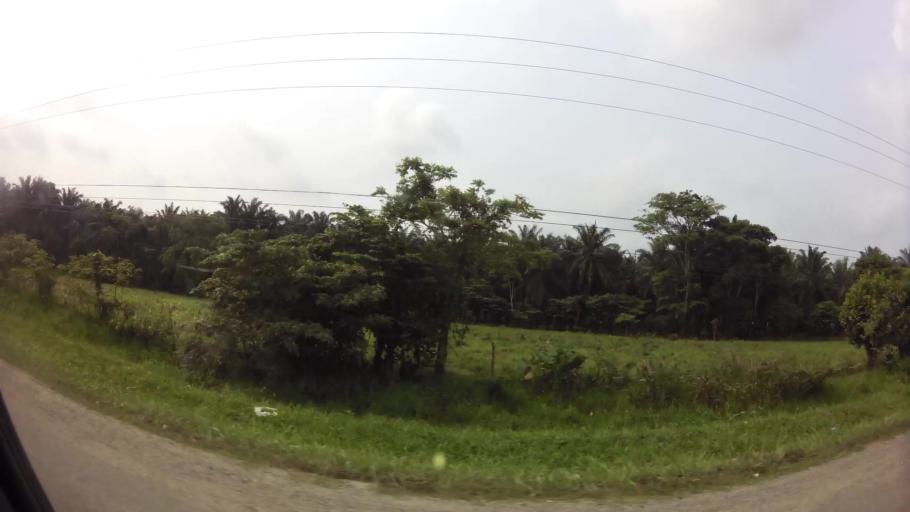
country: HN
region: Atlantida
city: Tela
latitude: 15.7652
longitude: -87.4705
